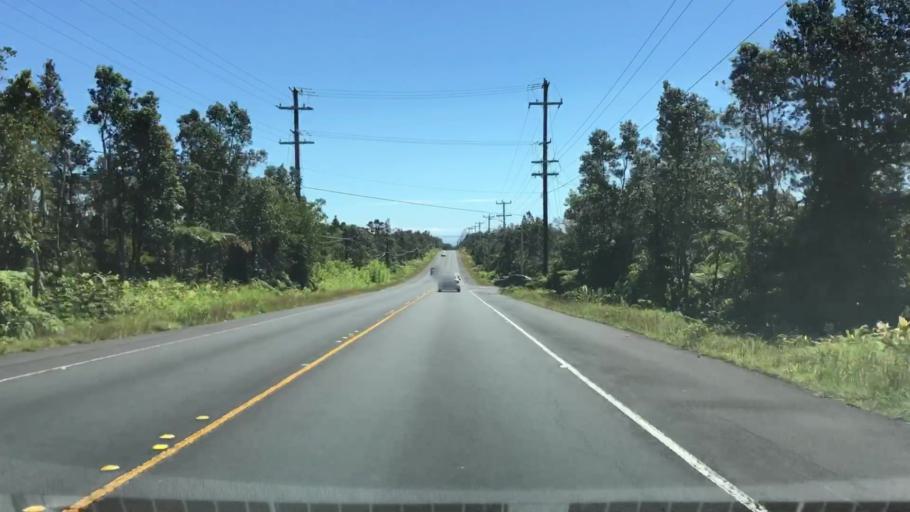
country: US
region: Hawaii
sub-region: Hawaii County
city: Volcano
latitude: 19.4523
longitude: -155.1865
